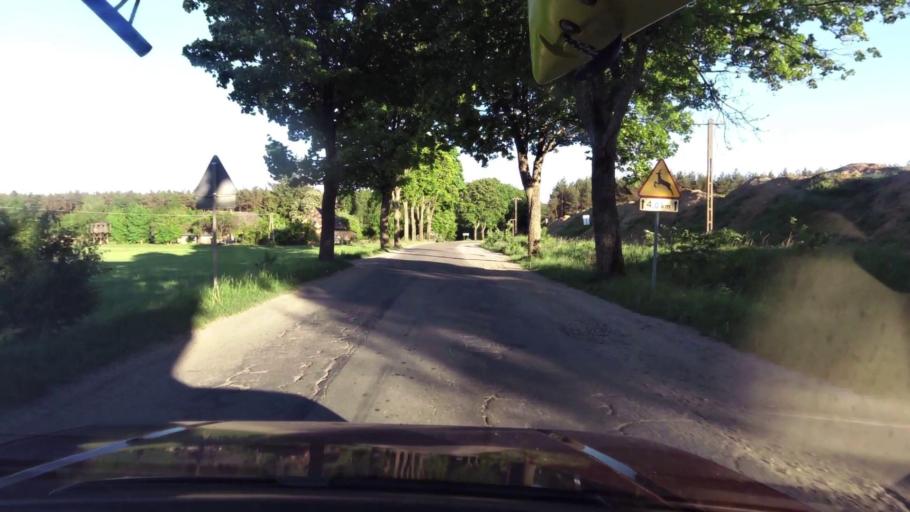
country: PL
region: West Pomeranian Voivodeship
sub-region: Powiat szczecinecki
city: Bialy Bor
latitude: 53.9343
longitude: 16.7968
